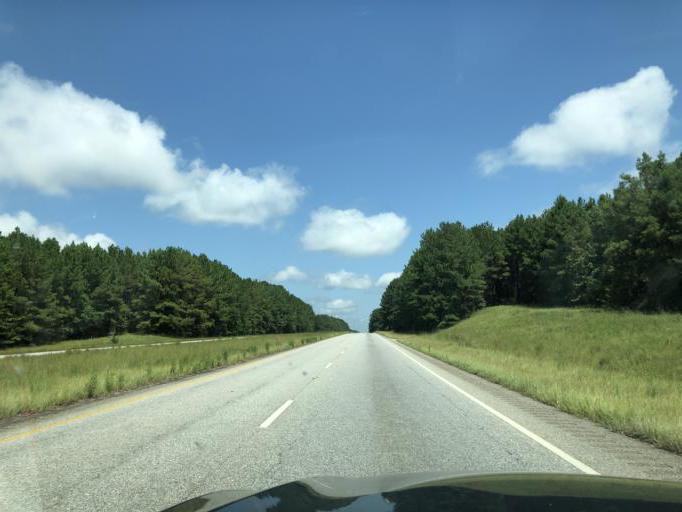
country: US
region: Alabama
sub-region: Henry County
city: Abbeville
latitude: 31.6590
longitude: -85.2800
